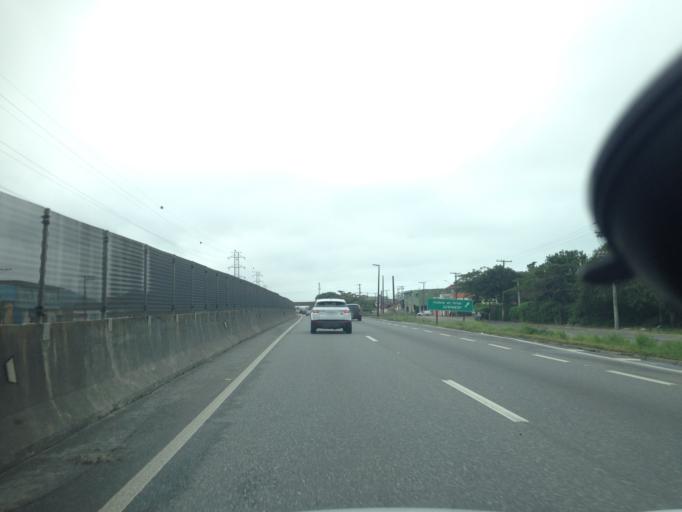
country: BR
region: Sao Paulo
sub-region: Itanhaem
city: Itanhaem
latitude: -24.1722
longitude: -46.7745
